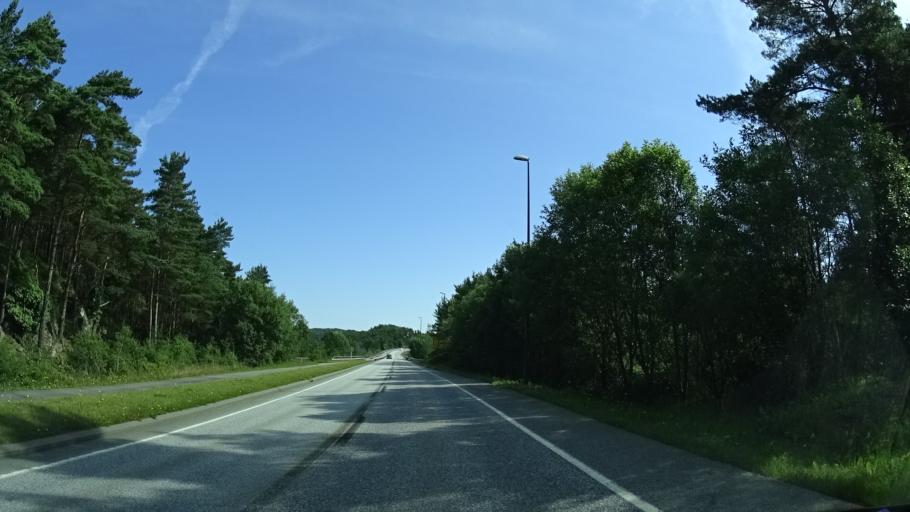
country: NO
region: Hordaland
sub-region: Bomlo
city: Mosterhamn
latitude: 59.7375
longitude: 5.3959
